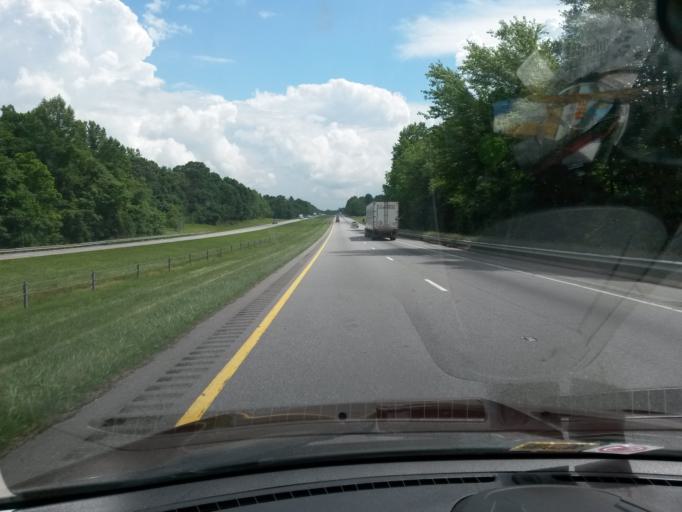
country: US
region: North Carolina
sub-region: Yadkin County
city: Jonesville
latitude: 36.0630
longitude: -80.8226
